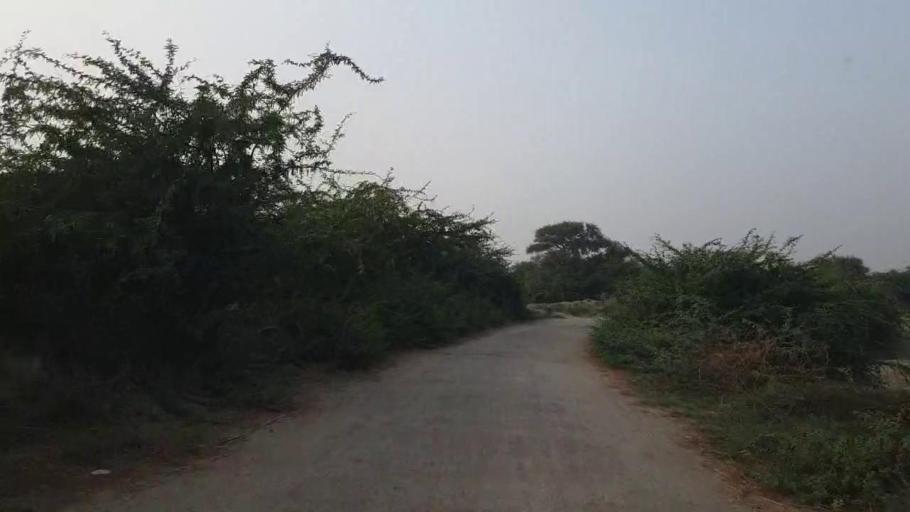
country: PK
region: Sindh
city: Mirpur Batoro
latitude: 24.6518
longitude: 68.3884
